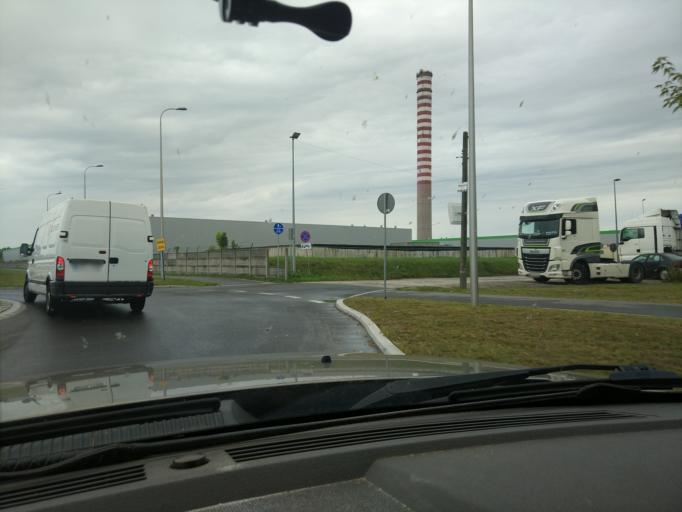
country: PL
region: Masovian Voivodeship
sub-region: Powiat pruszkowski
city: Brwinow
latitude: 52.1795
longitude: 20.7500
